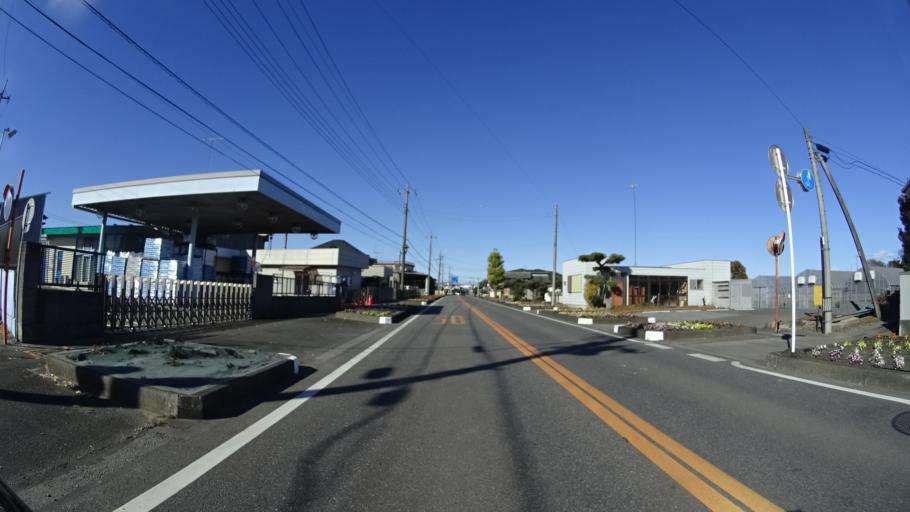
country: JP
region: Tochigi
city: Kanuma
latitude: 36.5012
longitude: 139.7521
